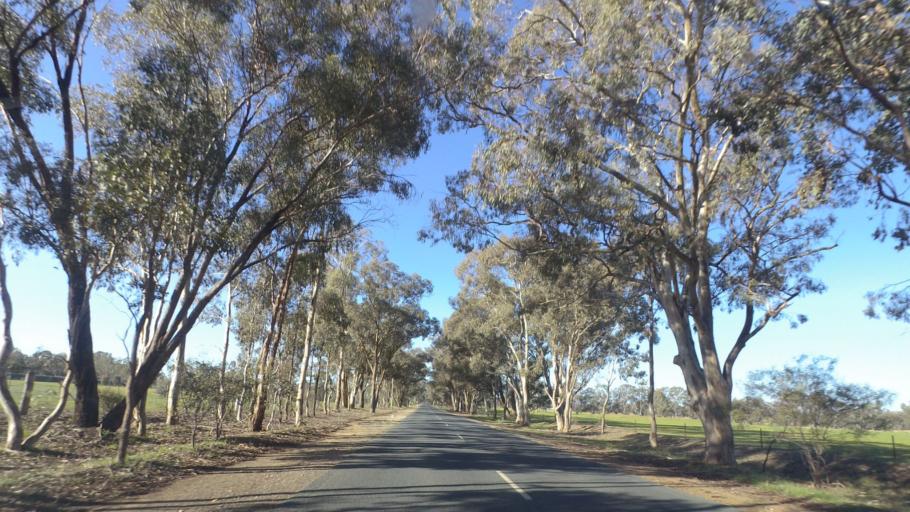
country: AU
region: Victoria
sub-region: Greater Bendigo
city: Epsom
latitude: -36.6615
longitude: 144.4580
